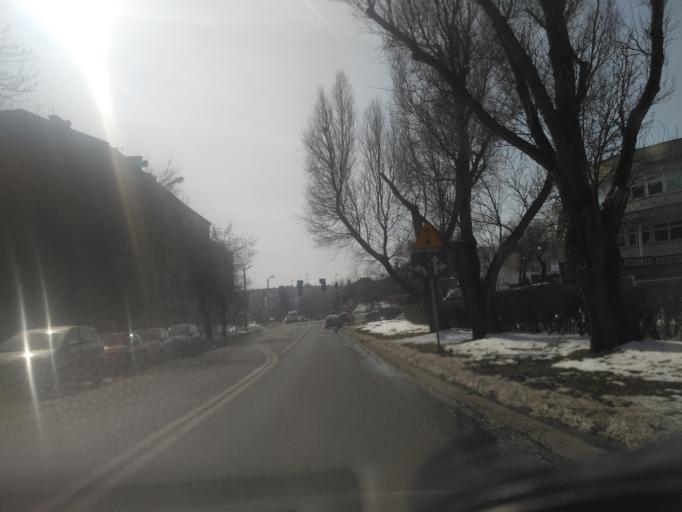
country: PL
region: Lublin Voivodeship
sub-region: Powiat lubelski
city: Lublin
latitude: 51.2565
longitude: 22.5644
